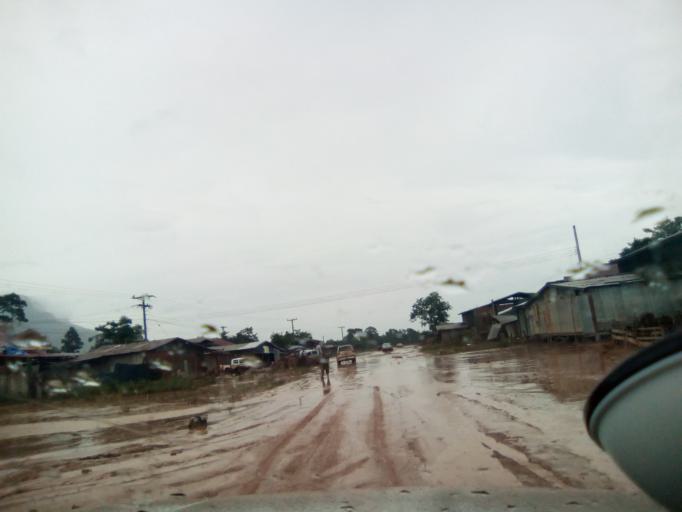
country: LA
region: Attapu
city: Attapu
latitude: 14.7015
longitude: 106.5287
